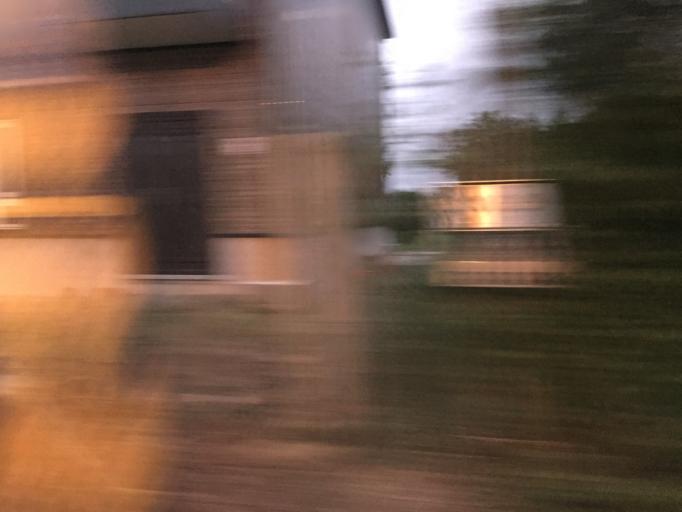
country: TW
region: Taiwan
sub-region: Yilan
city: Yilan
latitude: 24.7630
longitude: 121.7361
